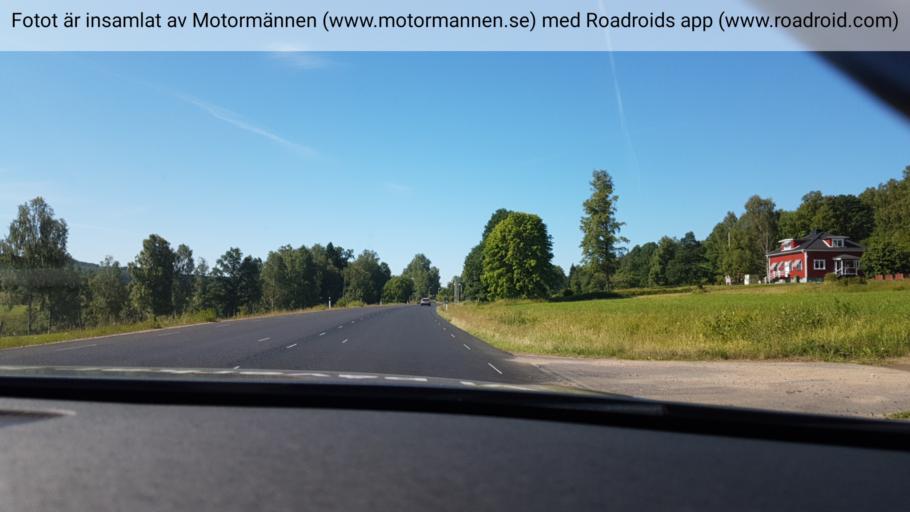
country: SE
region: Vaestra Goetaland
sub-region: Ulricehamns Kommun
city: Ulricehamn
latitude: 57.9085
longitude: 13.4755
